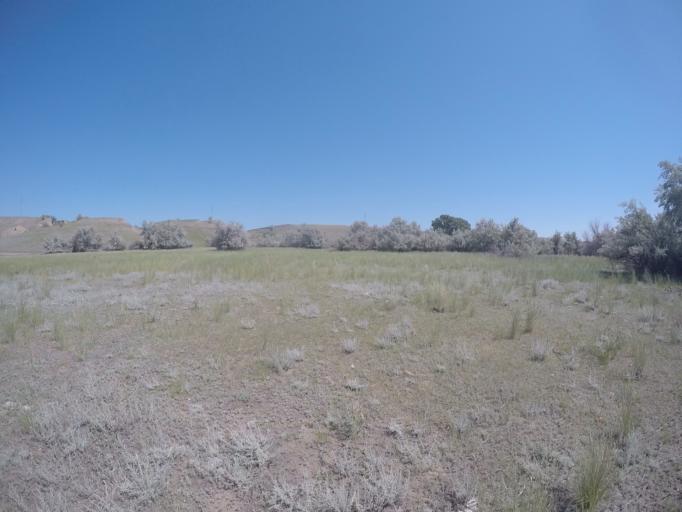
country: RU
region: Saratov
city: Krasnoarmeysk
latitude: 51.1500
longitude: 45.9314
